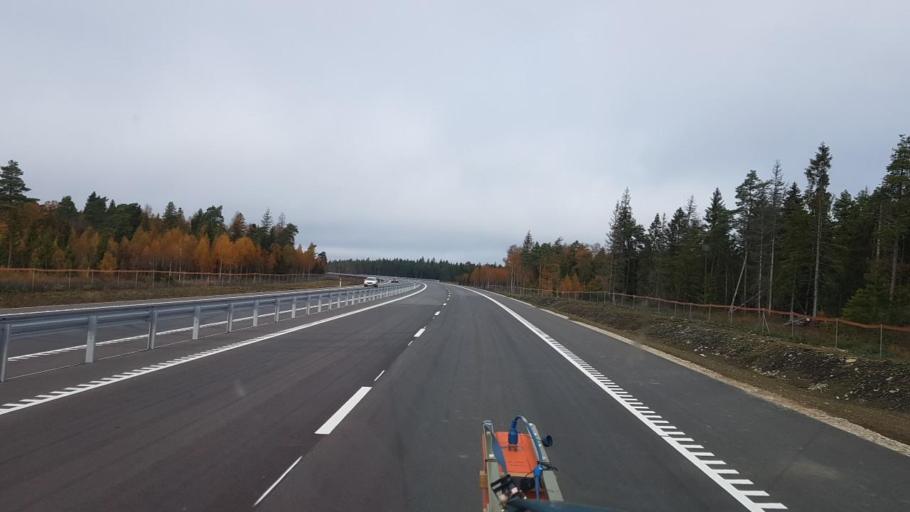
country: EE
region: Jaervamaa
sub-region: Paide linn
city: Paide
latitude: 59.0277
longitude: 25.5379
